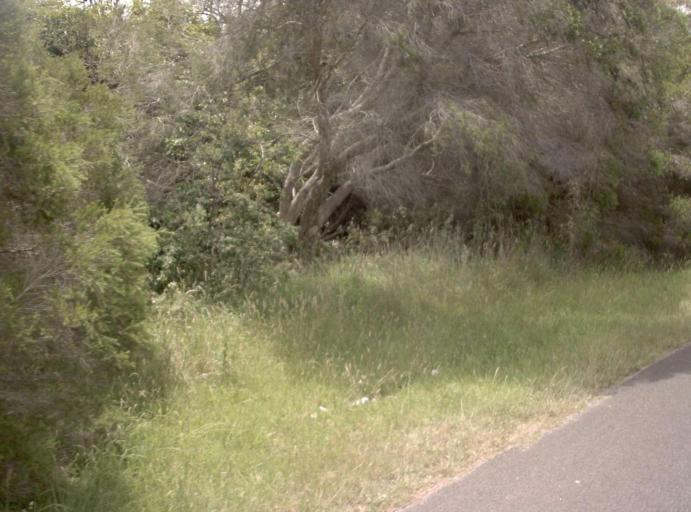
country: AU
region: Victoria
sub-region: Mornington Peninsula
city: Rosebud
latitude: -38.3649
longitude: 144.9164
